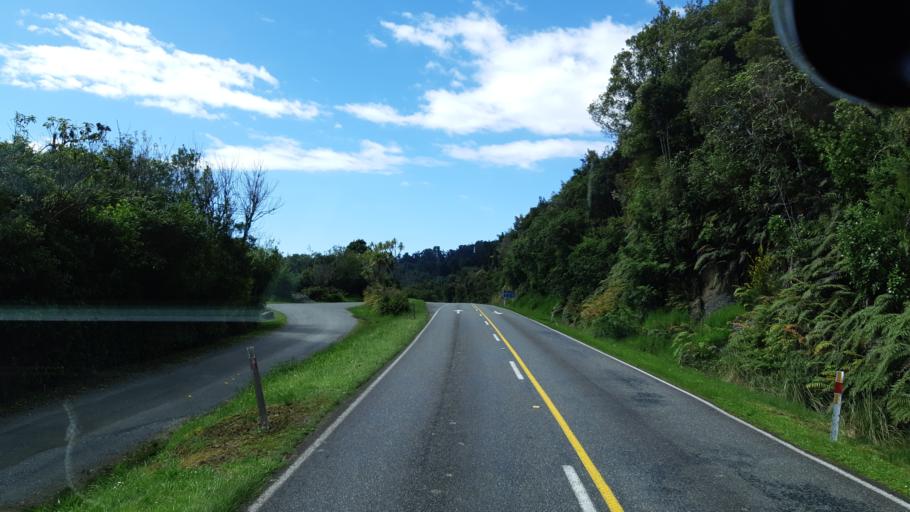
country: NZ
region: West Coast
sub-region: Westland District
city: Hokitika
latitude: -43.0594
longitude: 170.6347
